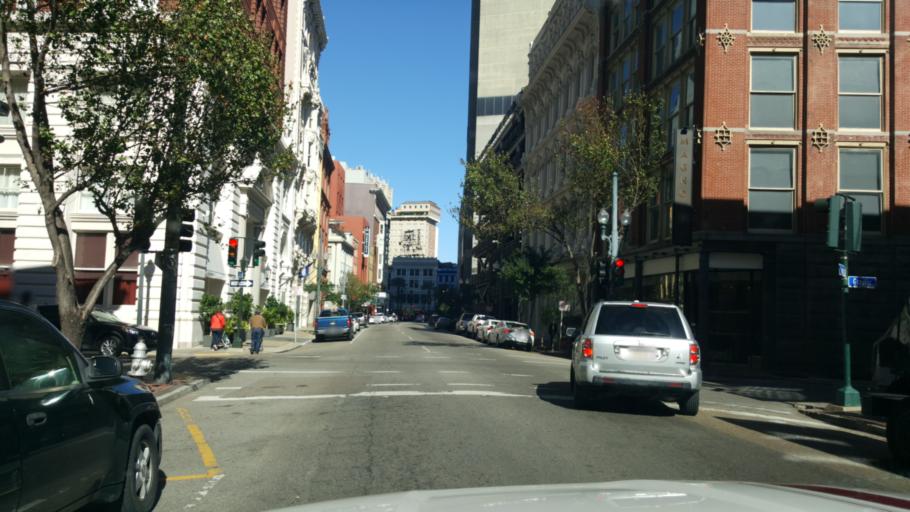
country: US
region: Louisiana
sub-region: Orleans Parish
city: New Orleans
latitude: 29.9509
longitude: -90.0690
